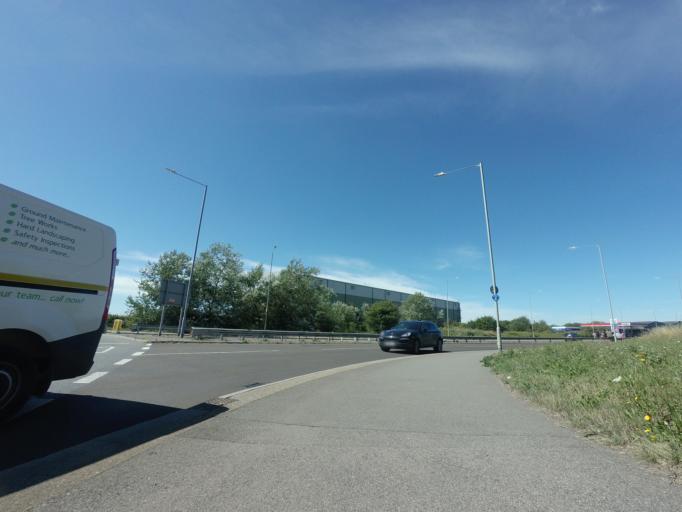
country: GB
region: England
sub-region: Kent
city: Sandwich
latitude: 51.3087
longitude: 1.3483
